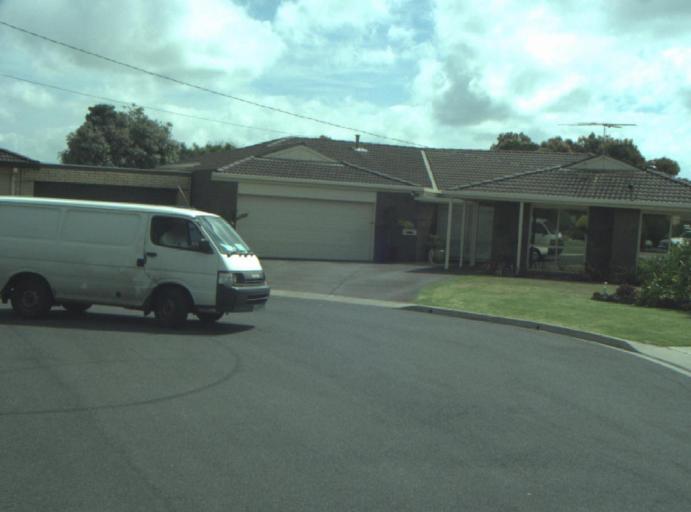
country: AU
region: Victoria
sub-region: Greater Geelong
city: Wandana Heights
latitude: -38.1783
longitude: 144.3293
